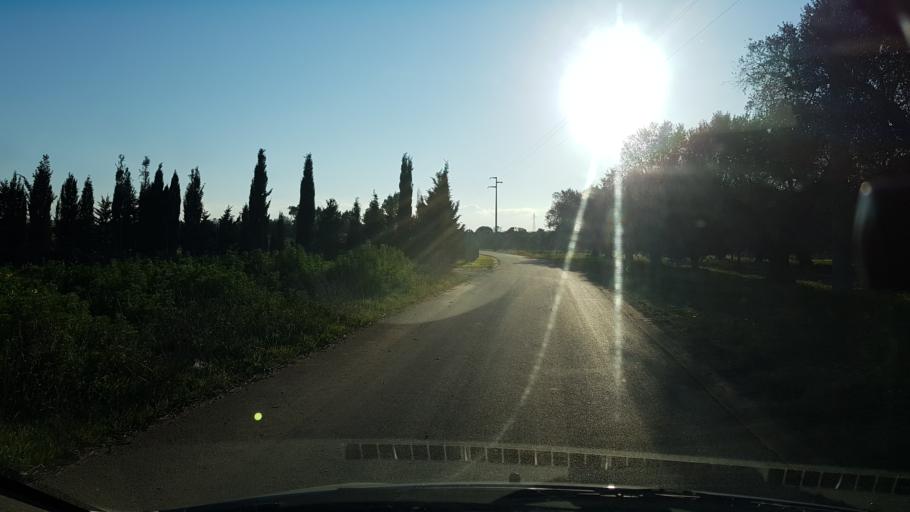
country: IT
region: Apulia
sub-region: Provincia di Brindisi
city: Mesagne
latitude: 40.5789
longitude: 17.8786
